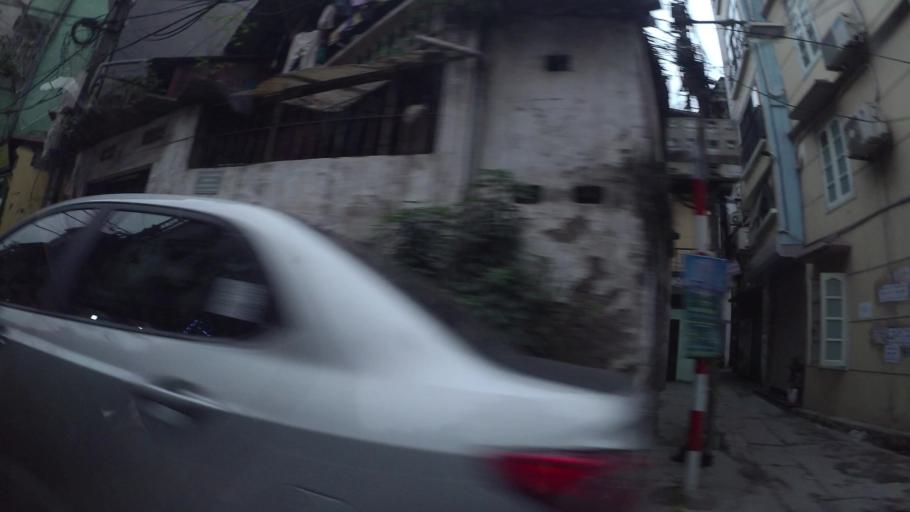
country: VN
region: Ha Noi
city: Hoan Kiem
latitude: 21.0197
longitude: 105.8635
